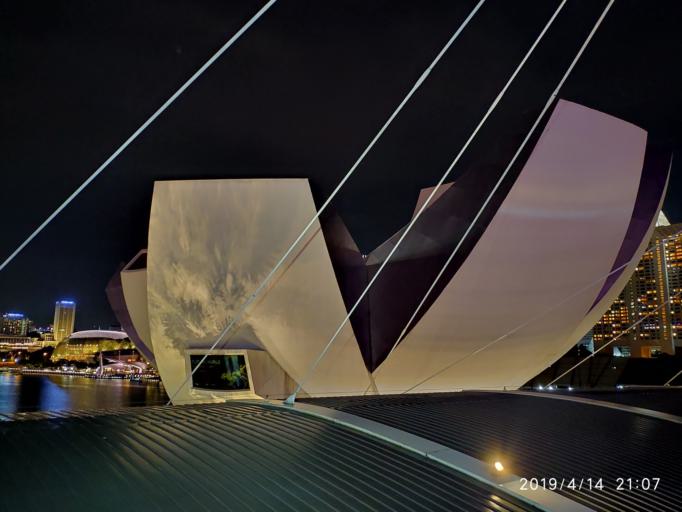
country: SG
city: Singapore
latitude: 1.2855
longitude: 103.8595
